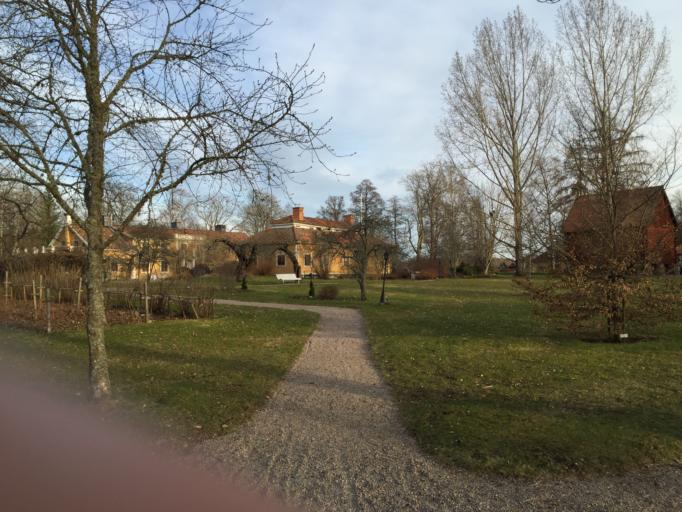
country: SE
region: Soedermanland
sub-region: Katrineholms Kommun
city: Katrineholm
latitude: 58.9714
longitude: 16.1923
